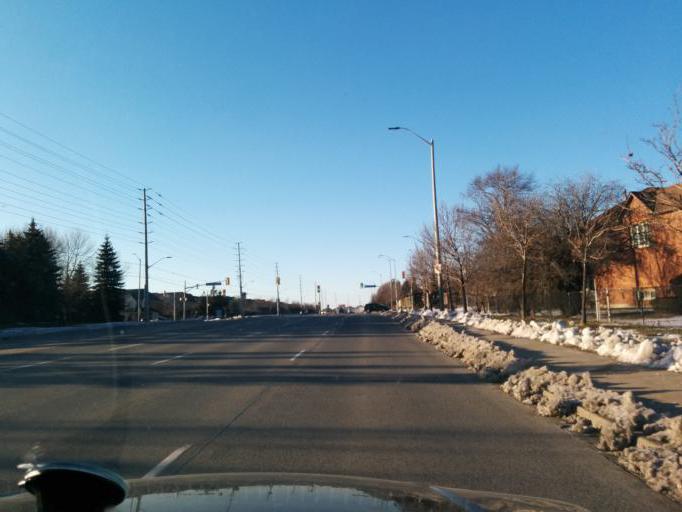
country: CA
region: Ontario
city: Mississauga
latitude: 43.5952
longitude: -79.6741
